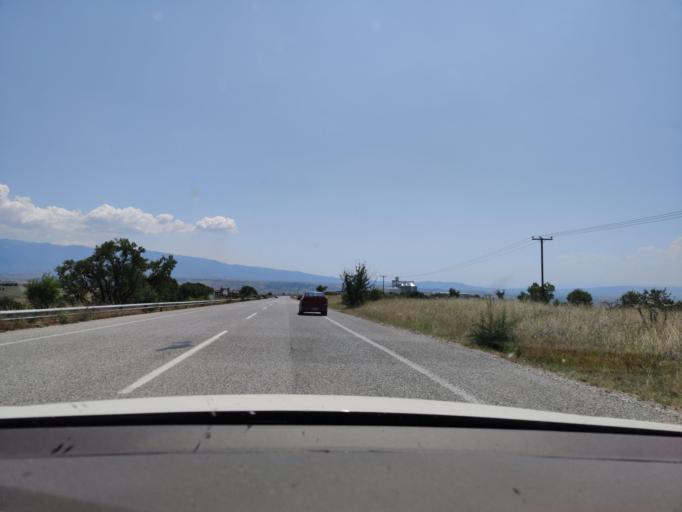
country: GR
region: Central Macedonia
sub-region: Nomos Serron
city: Nea Zichni
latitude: 41.0051
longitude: 23.8544
